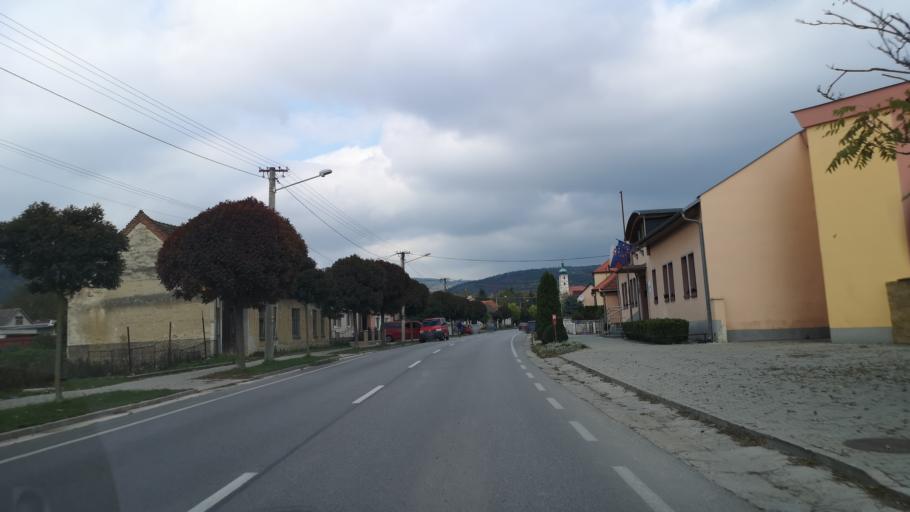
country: SK
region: Nitriansky
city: Cachtice
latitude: 48.7092
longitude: 17.7870
